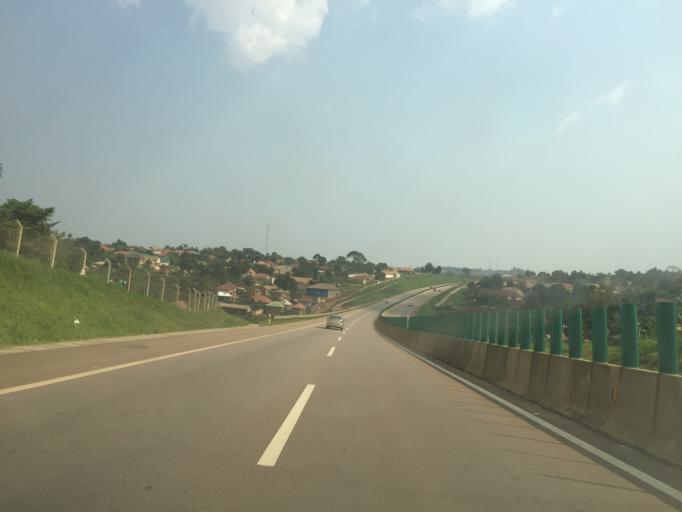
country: UG
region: Central Region
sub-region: Wakiso District
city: Kajansi
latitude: 0.2768
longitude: 32.5166
